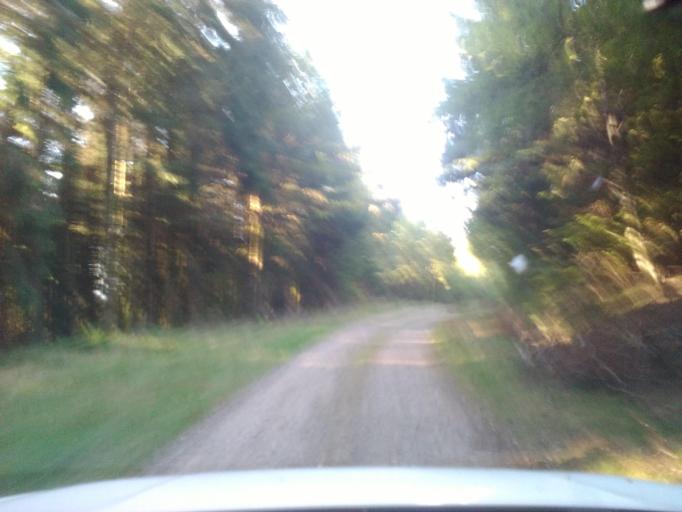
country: FR
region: Lorraine
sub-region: Departement des Vosges
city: Senones
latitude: 48.3447
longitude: 7.0631
